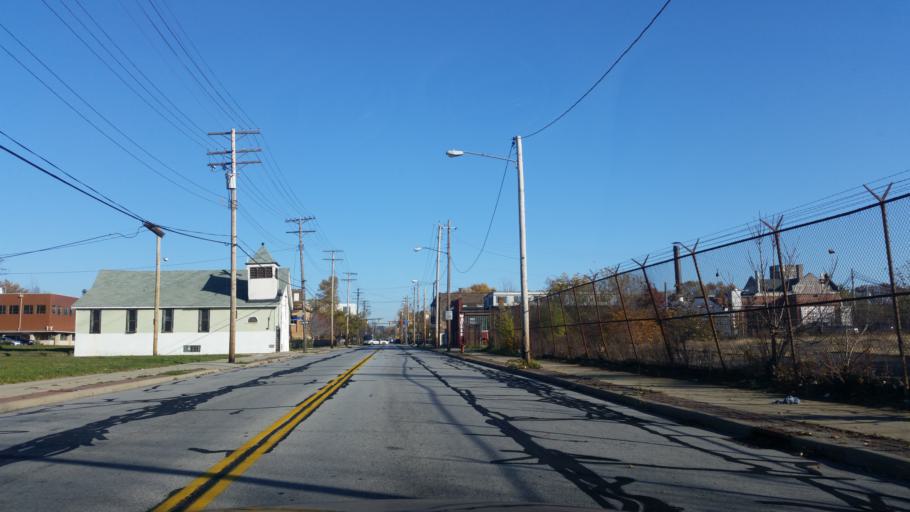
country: US
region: Ohio
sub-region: Cuyahoga County
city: Bratenahl
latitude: 41.4934
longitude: -81.6357
